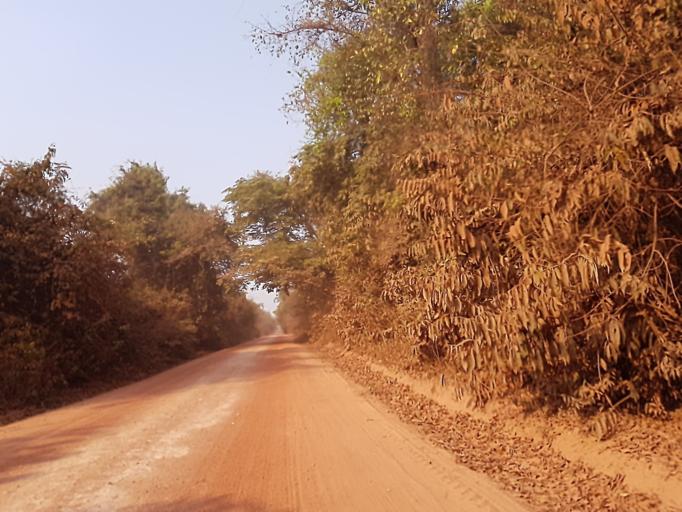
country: TH
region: Nong Khai
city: Phon Phisai
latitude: 18.0100
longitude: 102.9096
